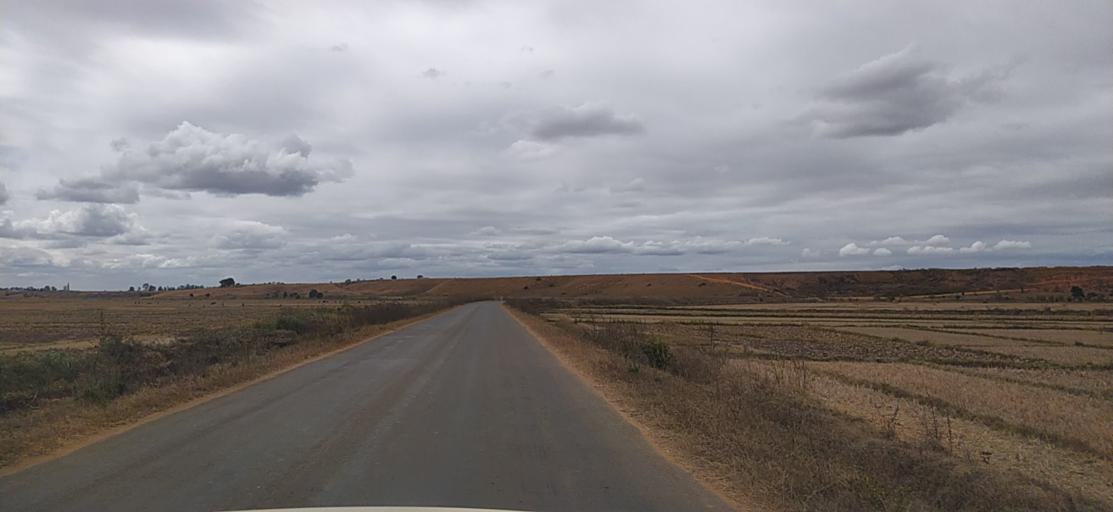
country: MG
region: Alaotra Mangoro
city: Ambatondrazaka
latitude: -17.9168
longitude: 48.2584
